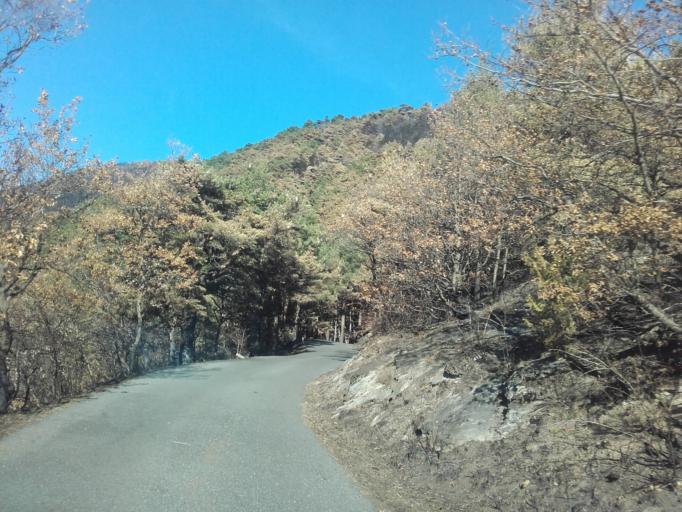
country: IT
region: Piedmont
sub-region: Provincia di Torino
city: Mompantero
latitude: 45.1551
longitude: 7.0507
